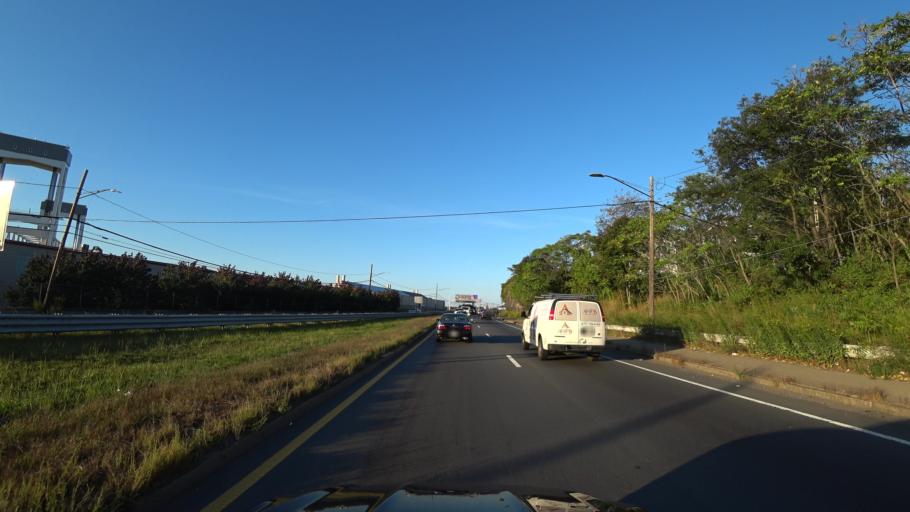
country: US
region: Massachusetts
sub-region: Suffolk County
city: Chelsea
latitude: 42.3837
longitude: -71.0210
